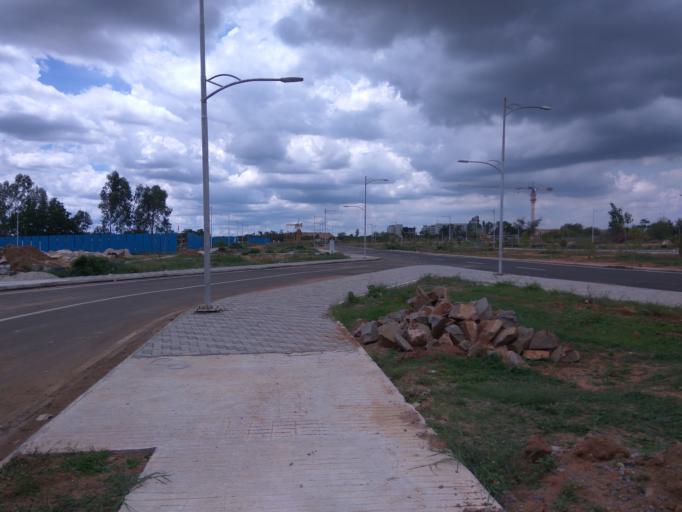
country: IN
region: Telangana
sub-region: Medak
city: Sangareddi
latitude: 17.5855
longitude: 78.1201
